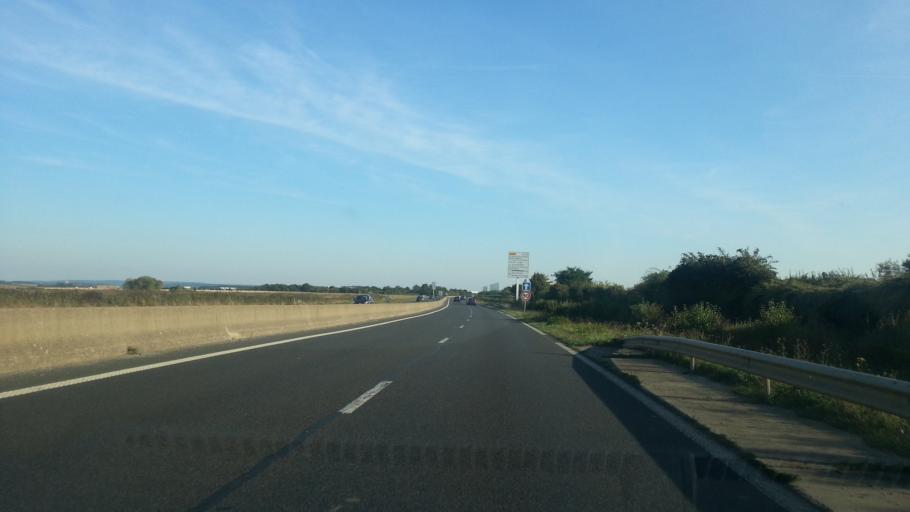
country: FR
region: Picardie
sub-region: Departement de l'Oise
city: Tille
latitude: 49.4481
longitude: 2.1045
